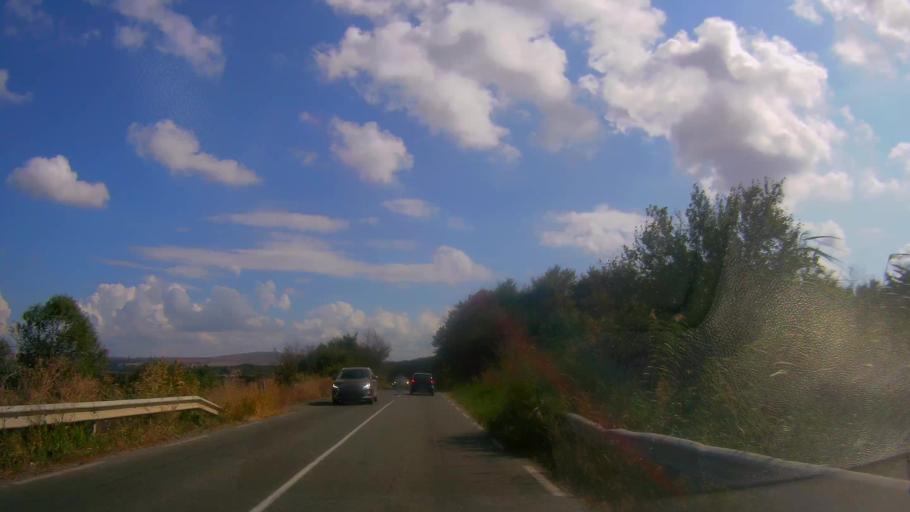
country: BG
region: Burgas
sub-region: Obshtina Kameno
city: Kameno
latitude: 42.4890
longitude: 27.3392
